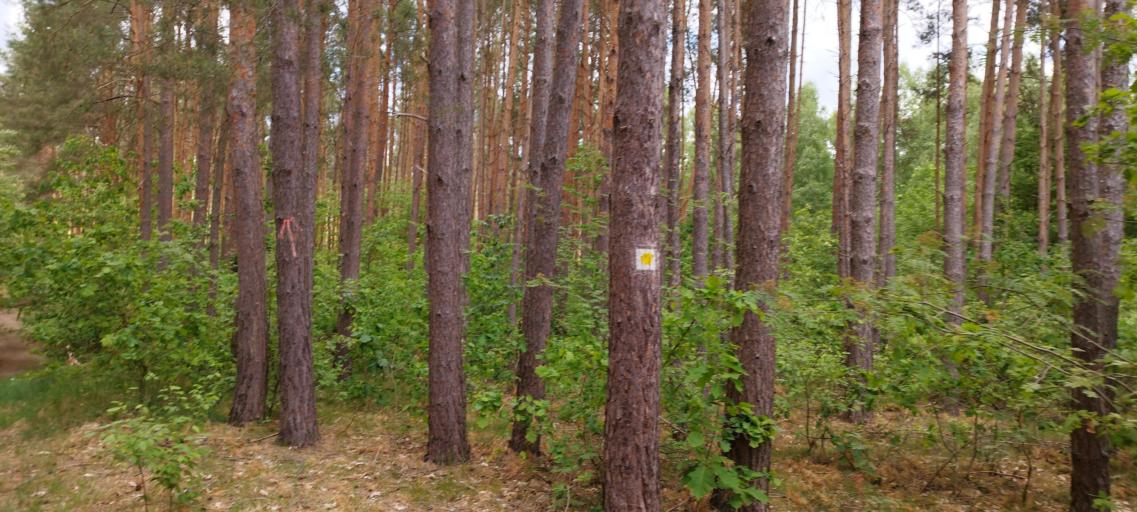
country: DE
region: Brandenburg
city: Wandlitz
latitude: 52.7126
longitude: 13.4273
